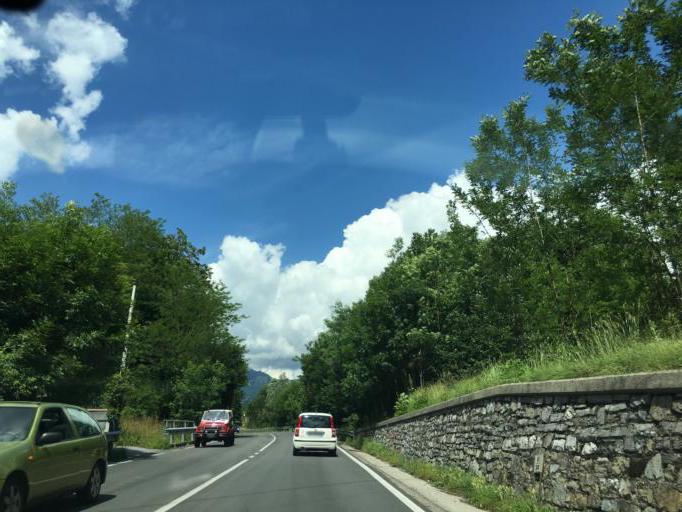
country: IT
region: Lombardy
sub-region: Provincia di Como
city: Codogna-Cardano
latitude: 46.0274
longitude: 9.2040
